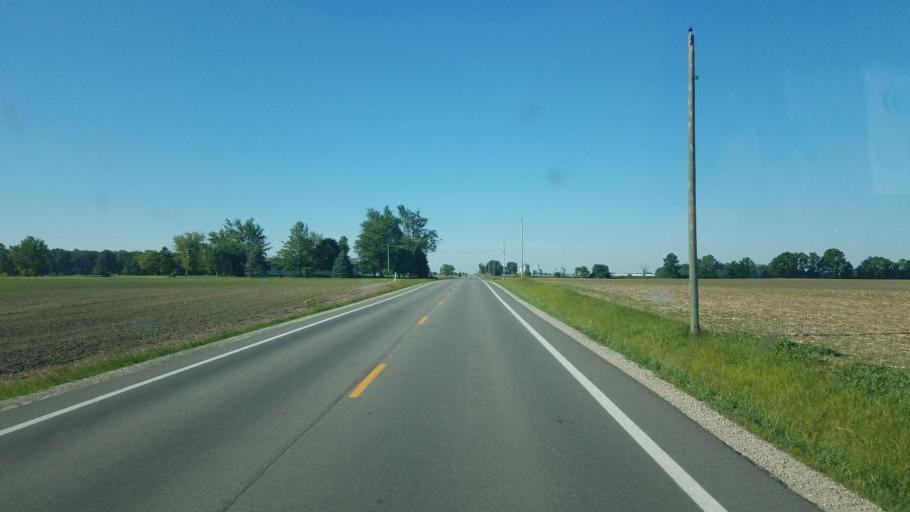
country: US
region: Ohio
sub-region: Crawford County
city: Bucyrus
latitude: 40.7574
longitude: -82.9884
